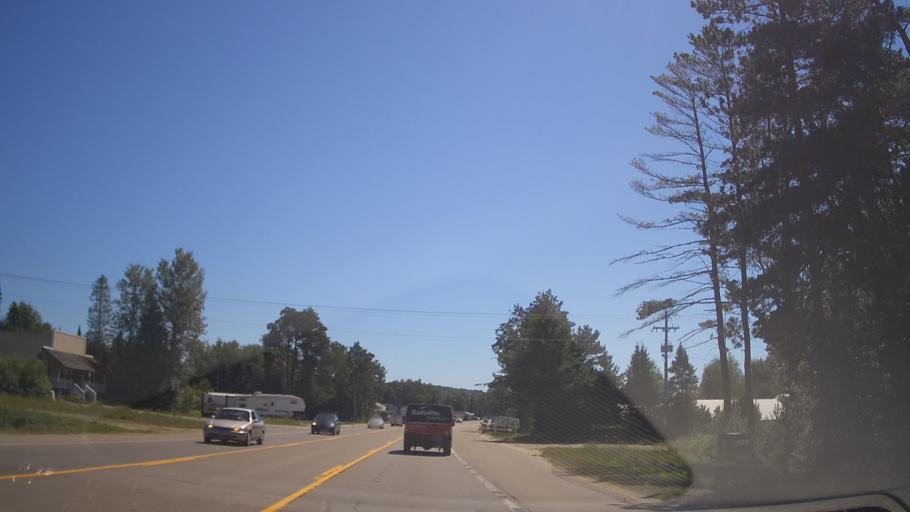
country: US
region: Michigan
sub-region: Emmet County
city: Petoskey
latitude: 45.4067
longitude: -84.8712
